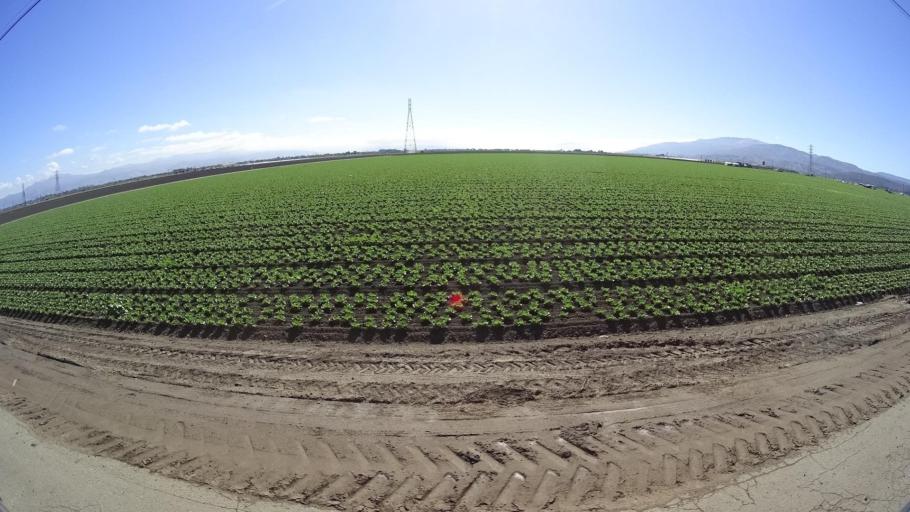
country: US
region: California
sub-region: Monterey County
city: Boronda
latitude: 36.6701
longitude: -121.7045
